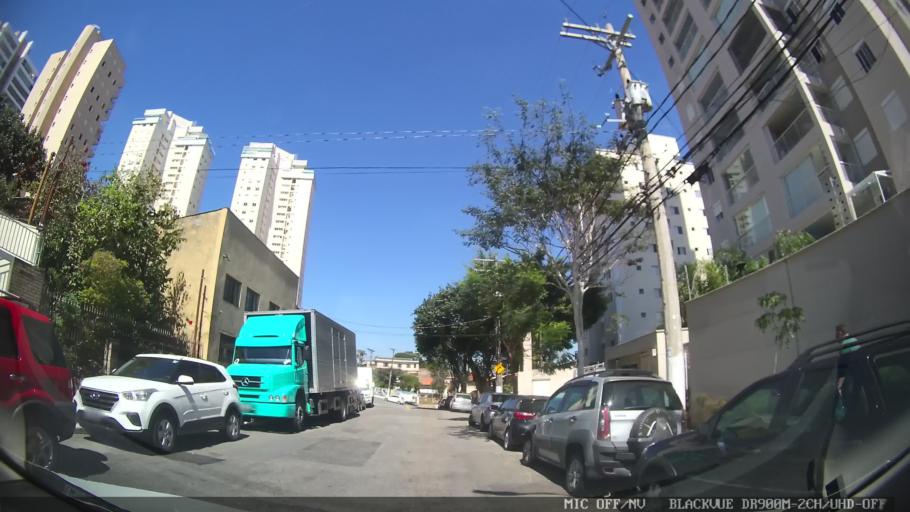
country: BR
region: Sao Paulo
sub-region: Sao Paulo
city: Sao Paulo
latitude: -23.4988
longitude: -46.6432
